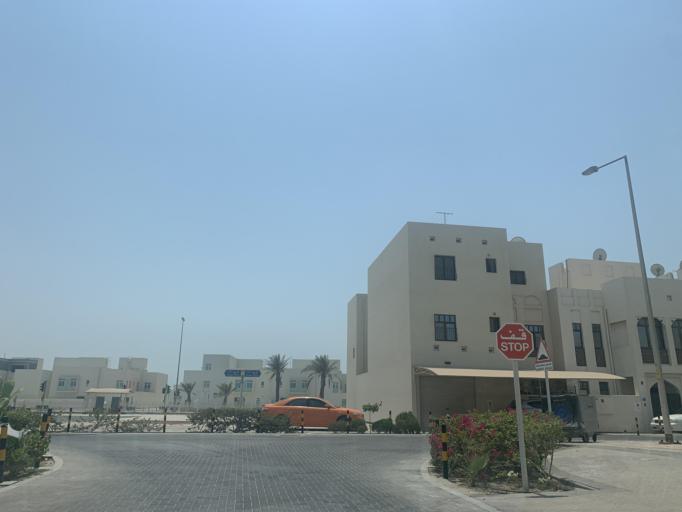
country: BH
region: Muharraq
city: Al Hadd
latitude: 26.2342
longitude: 50.6698
